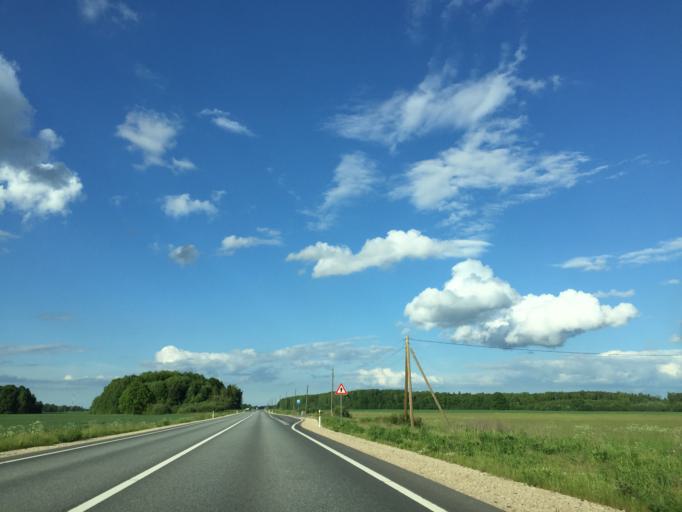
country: LV
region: Dobeles Rajons
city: Dobele
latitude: 56.7684
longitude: 23.3332
